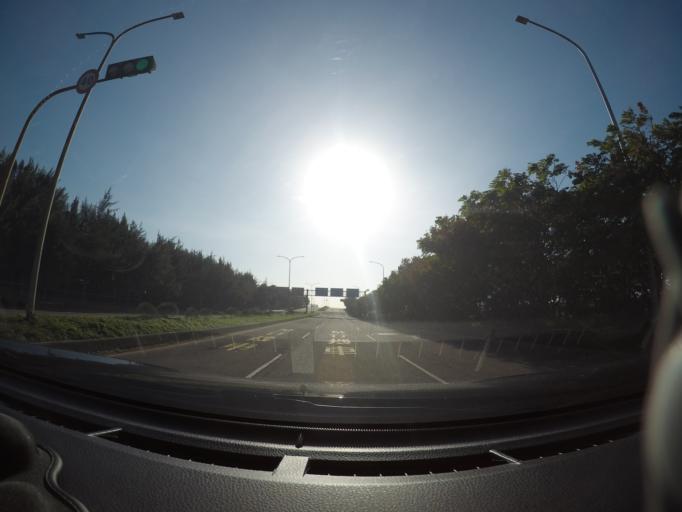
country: TW
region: Taiwan
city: Taoyuan City
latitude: 25.1006
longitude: 121.2535
